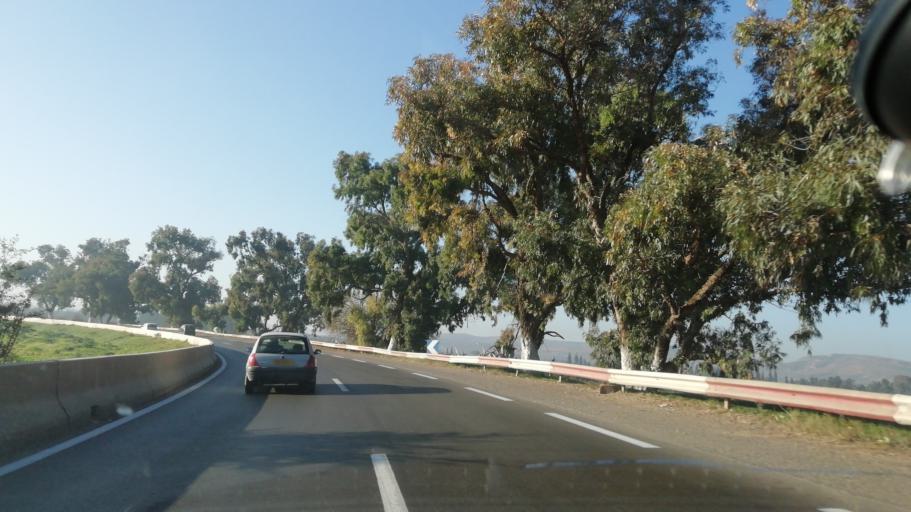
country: DZ
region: Tlemcen
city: Remchi
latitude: 35.1058
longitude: -1.4422
